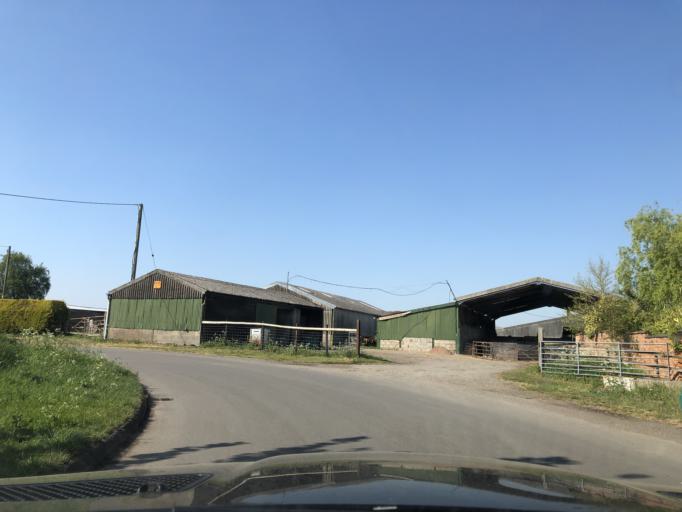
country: GB
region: England
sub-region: Warwickshire
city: Warwick
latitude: 52.2888
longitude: -1.6243
